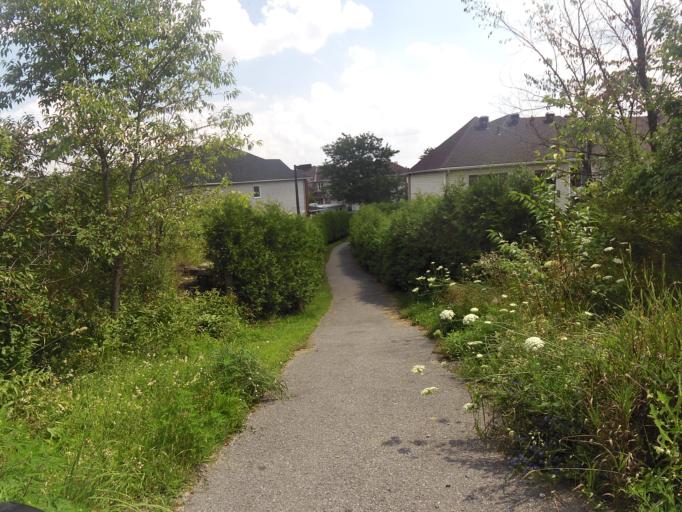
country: CA
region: Ontario
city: Bells Corners
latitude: 45.3207
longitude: -75.9221
